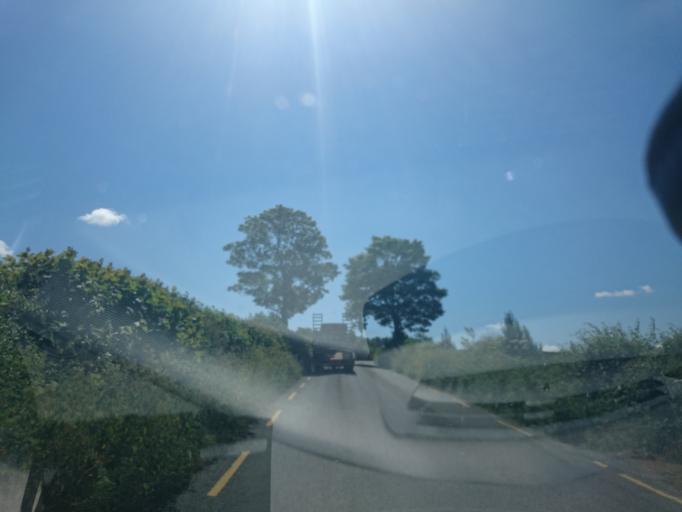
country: IE
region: Leinster
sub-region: Kilkenny
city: Graiguenamanagh
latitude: 52.6078
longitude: -6.9925
